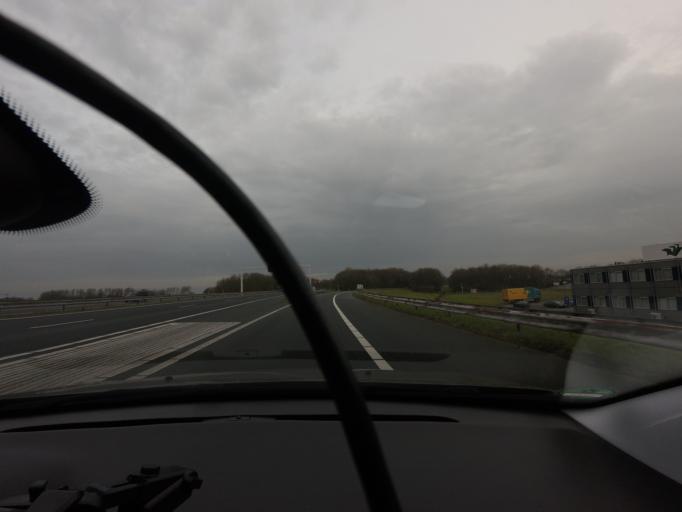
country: NL
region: North Holland
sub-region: Gemeente Hollands Kroon
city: Den Oever
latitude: 52.9254
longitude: 5.0353
